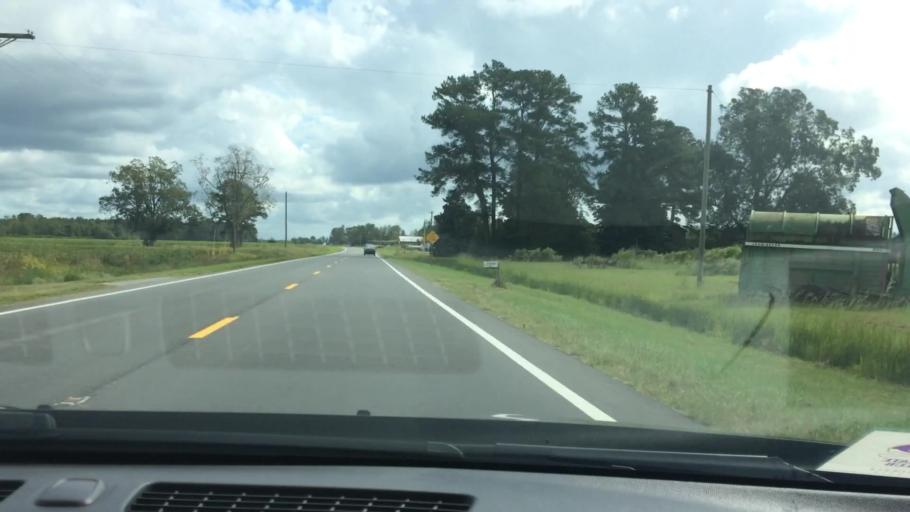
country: US
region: North Carolina
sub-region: Pitt County
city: Farmville
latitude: 35.5617
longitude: -77.5619
